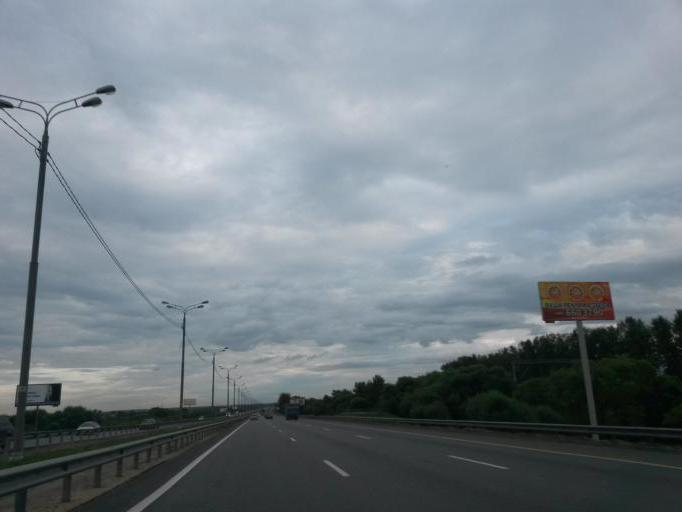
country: RU
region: Moskovskaya
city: Yam
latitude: 55.5129
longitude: 37.7145
